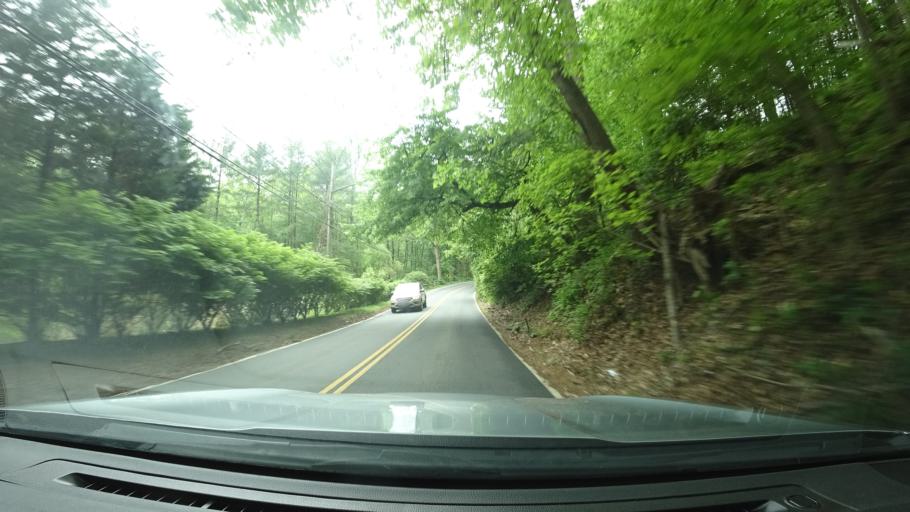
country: US
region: Virginia
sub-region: Fairfax County
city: Oakton
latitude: 38.8807
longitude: -77.3377
